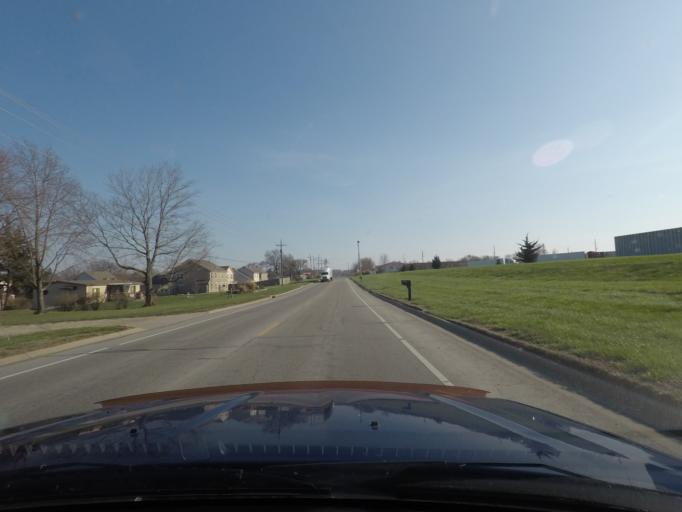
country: US
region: Kansas
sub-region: Douglas County
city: Lawrence
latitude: 38.9954
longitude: -95.2605
